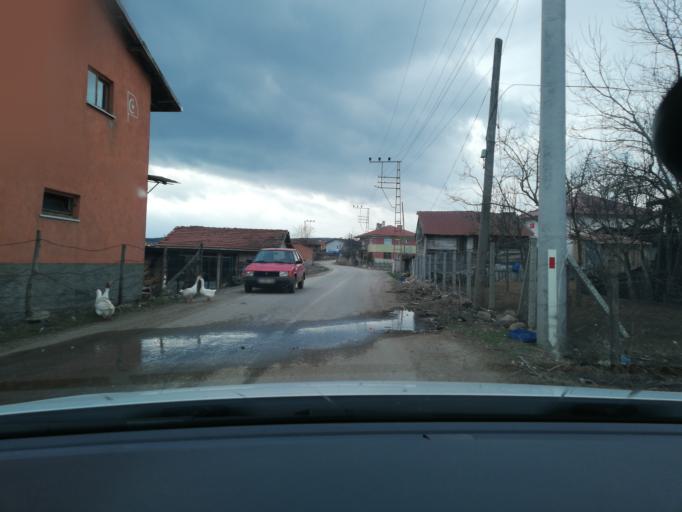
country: TR
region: Bolu
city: Gerede
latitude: 40.6910
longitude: 32.2144
